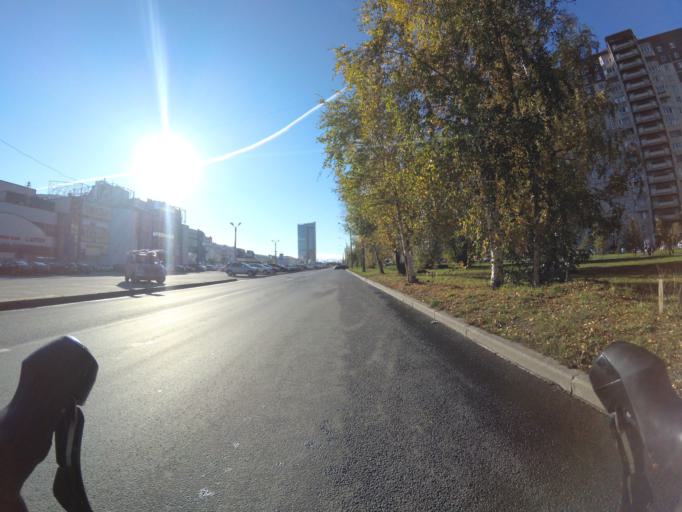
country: RU
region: Leningrad
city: Untolovo
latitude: 59.9921
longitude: 30.2044
